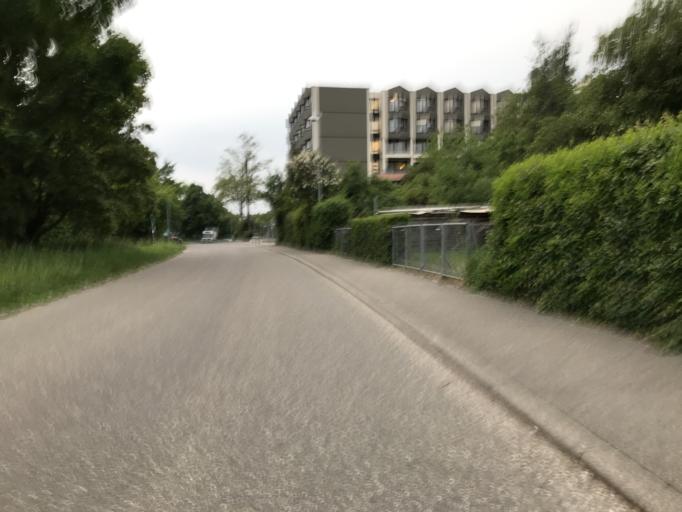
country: DE
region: Baden-Wuerttemberg
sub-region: Regierungsbezirk Stuttgart
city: Korntal
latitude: 48.8161
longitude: 9.1245
